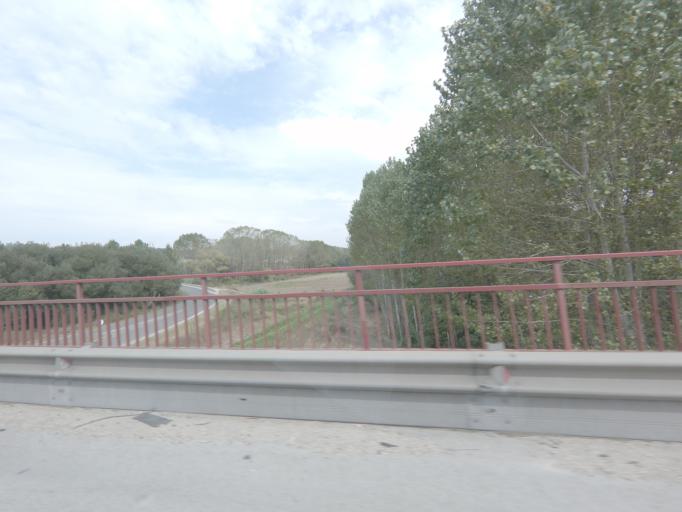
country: PT
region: Leiria
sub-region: Leiria
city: Caranguejeira
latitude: 39.8056
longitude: -8.7418
